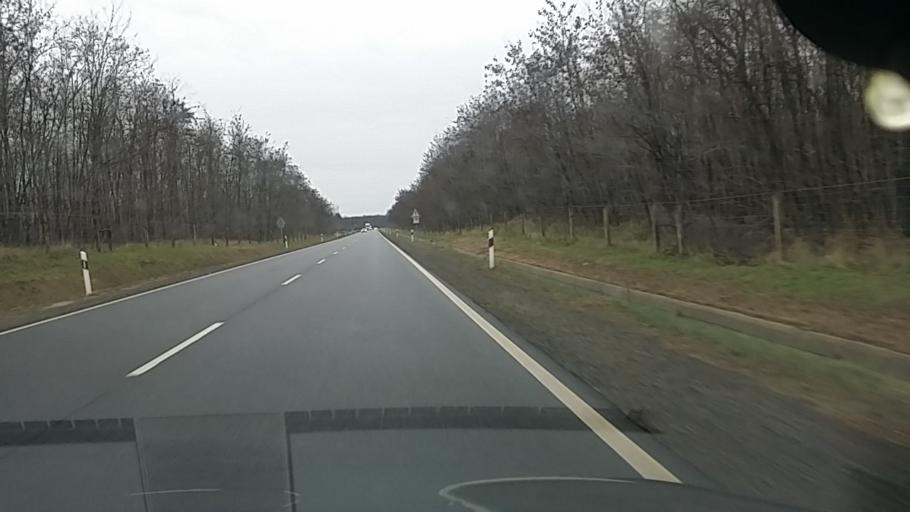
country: HU
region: Hajdu-Bihar
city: Hajduhadhaz
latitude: 47.6225
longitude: 21.6391
